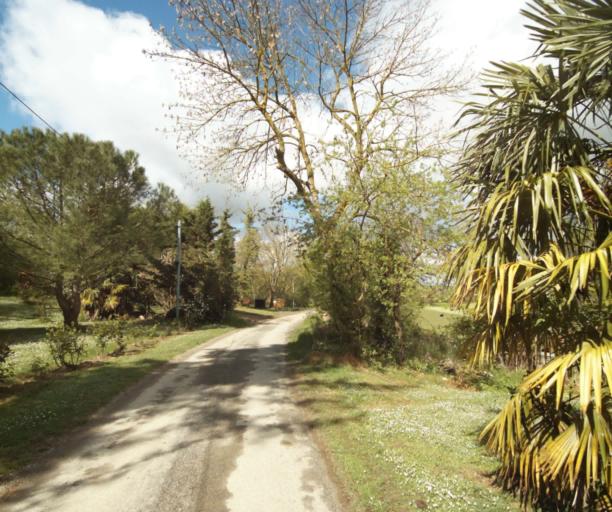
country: FR
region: Midi-Pyrenees
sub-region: Departement de l'Ariege
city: Saverdun
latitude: 43.1828
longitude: 1.5434
